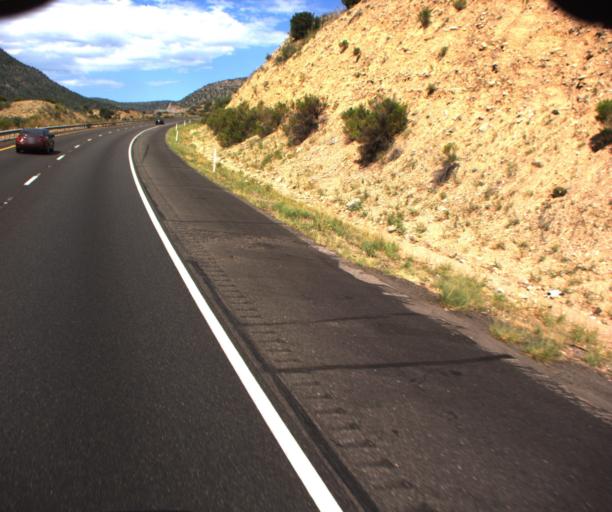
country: US
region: Arizona
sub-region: Yavapai County
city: Camp Verde
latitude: 34.5389
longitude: -111.9131
